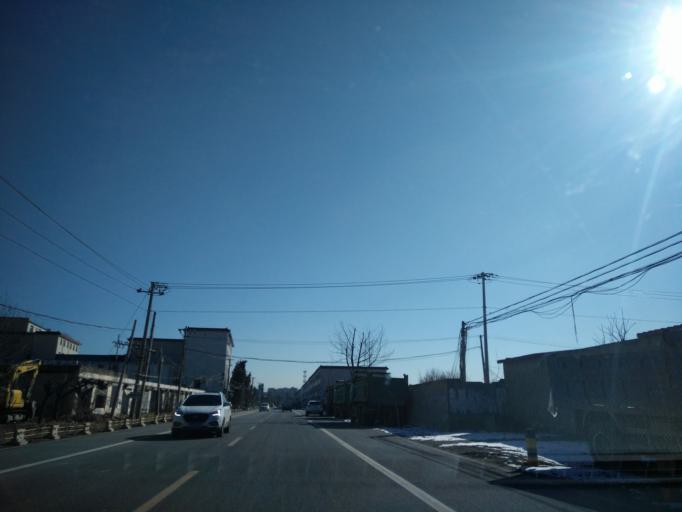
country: CN
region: Beijing
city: Yinghai
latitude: 39.7535
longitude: 116.4602
